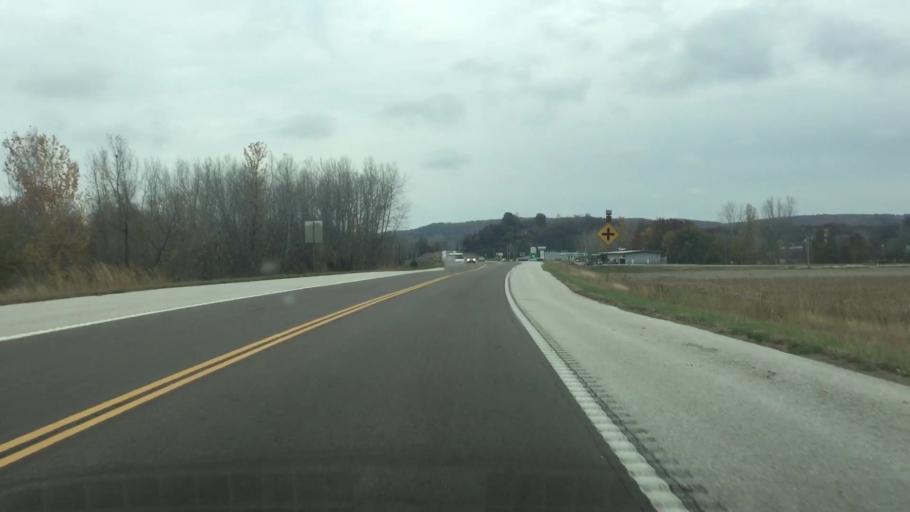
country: US
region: Missouri
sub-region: Gasconade County
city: Hermann
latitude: 38.7262
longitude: -91.4453
